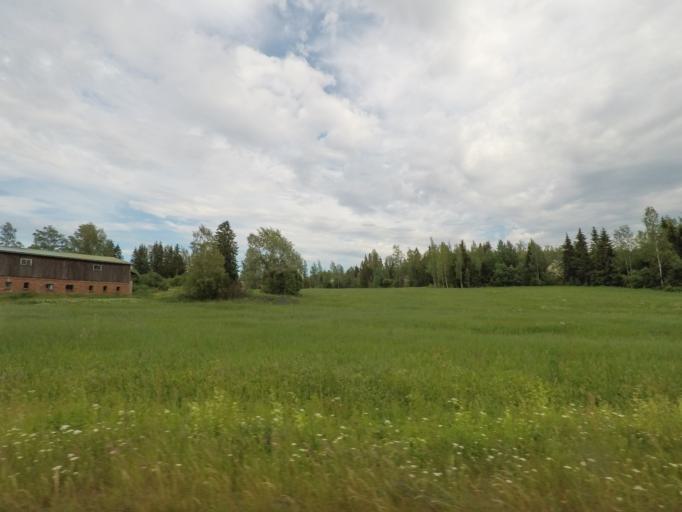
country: FI
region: Paijanne Tavastia
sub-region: Lahti
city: Hollola
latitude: 60.8195
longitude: 25.4852
